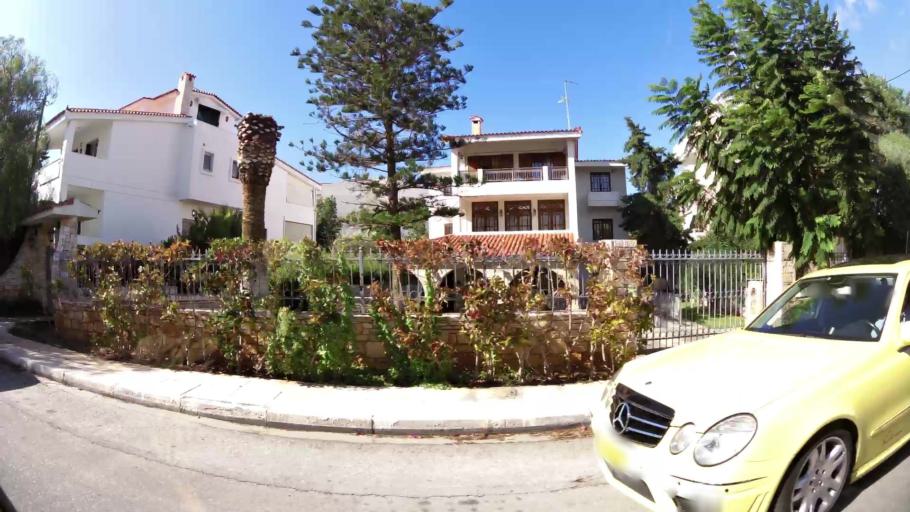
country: GR
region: Attica
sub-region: Nomarchia Anatolikis Attikis
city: Voula
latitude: 37.8301
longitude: 23.7762
